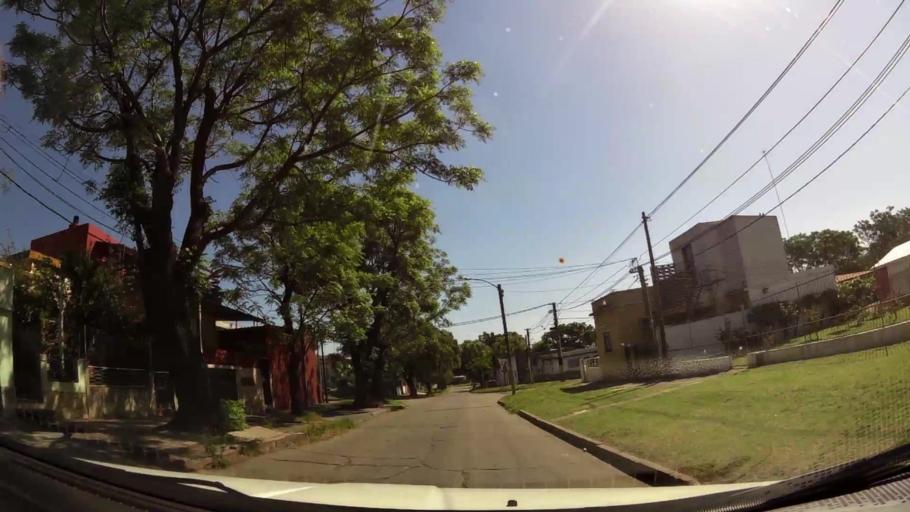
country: UY
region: Montevideo
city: Montevideo
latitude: -34.8536
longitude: -56.2383
